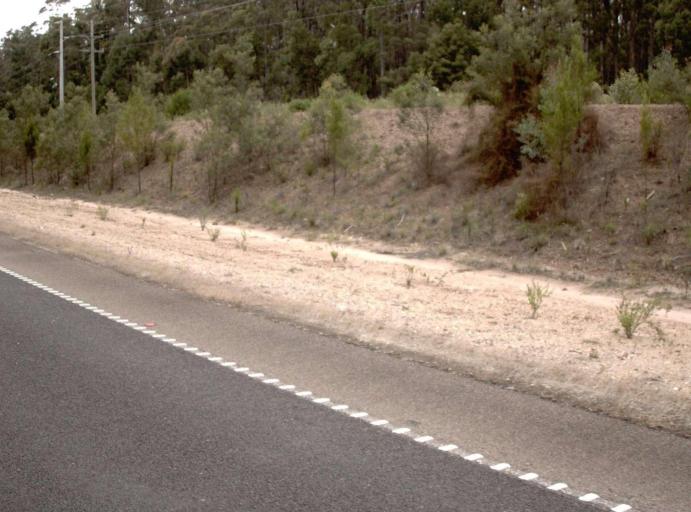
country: AU
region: Victoria
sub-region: East Gippsland
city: Lakes Entrance
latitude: -37.7074
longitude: 148.0690
